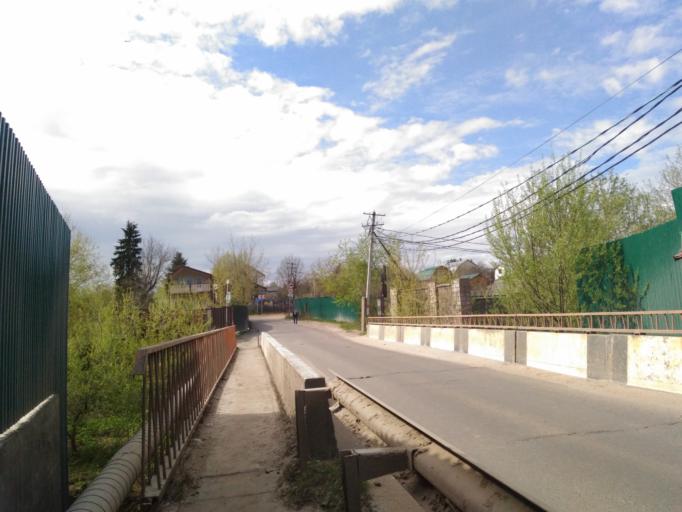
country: RU
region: Moskovskaya
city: Nakhabino
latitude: 55.8487
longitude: 37.1528
